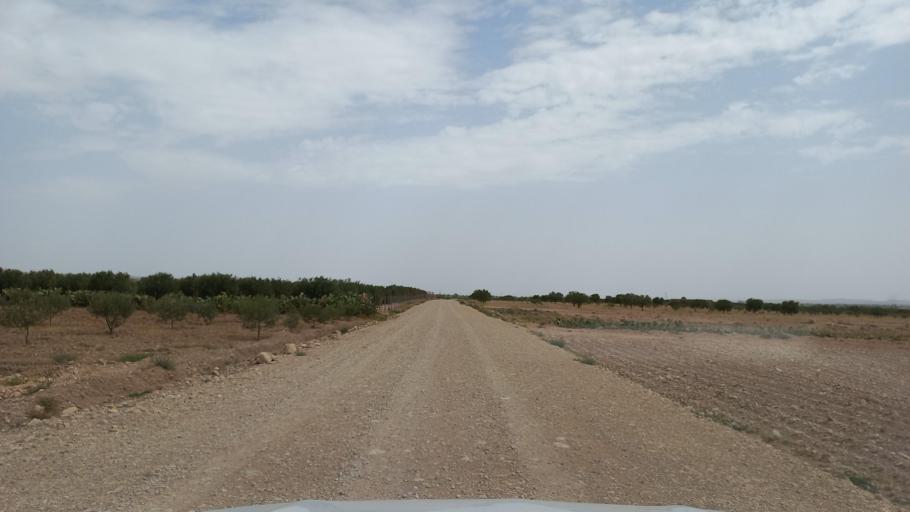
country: TN
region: Al Qasrayn
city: Kasserine
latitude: 35.2802
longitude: 9.0120
